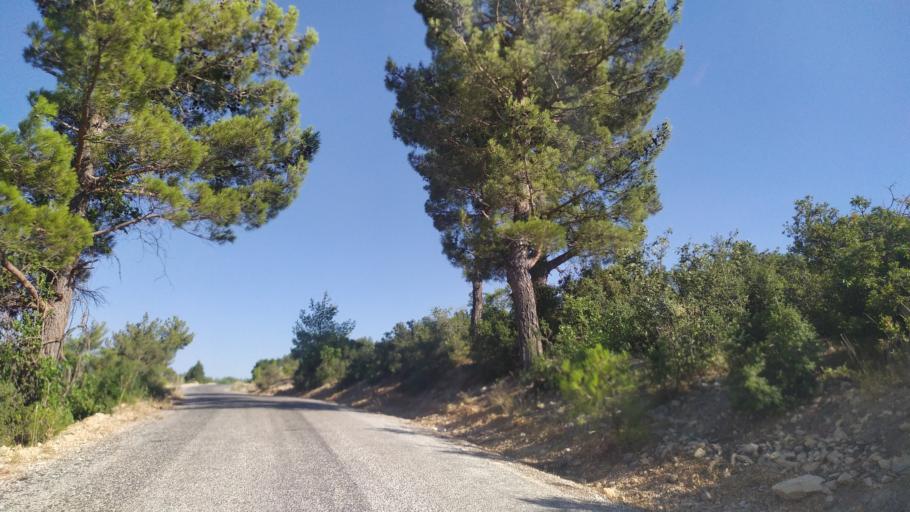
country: TR
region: Mersin
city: Mut
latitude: 36.7006
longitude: 33.4789
